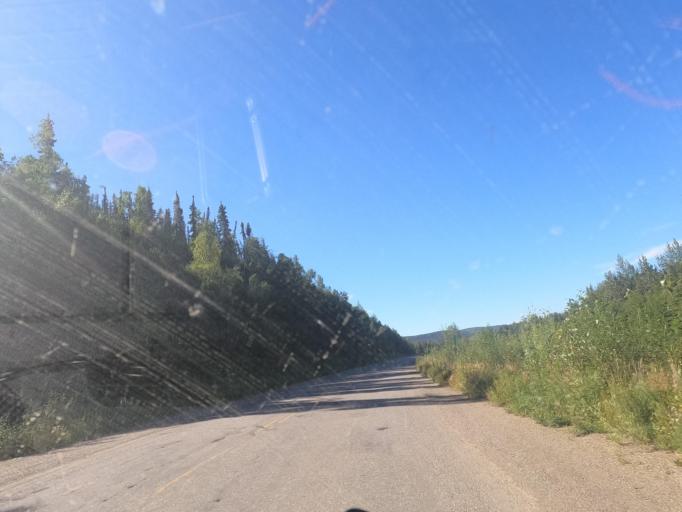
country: CA
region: Yukon
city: Dawson City
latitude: 63.9513
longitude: -138.6670
